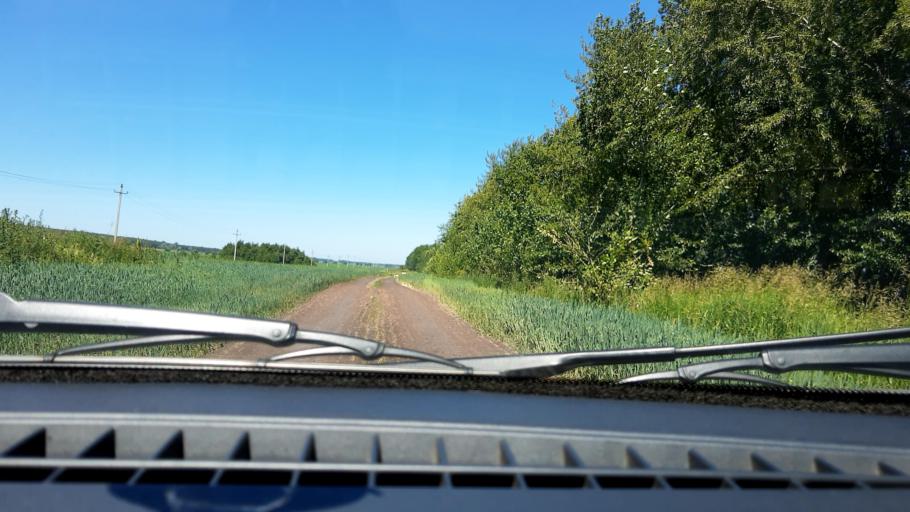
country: RU
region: Bashkortostan
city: Mikhaylovka
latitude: 54.8557
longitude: 55.9462
